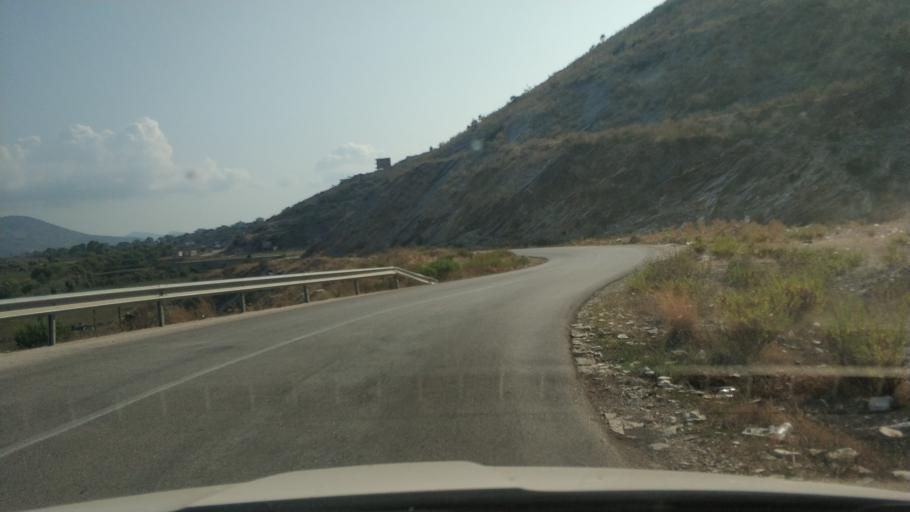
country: AL
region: Vlore
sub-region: Rrethi i Sarandes
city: Sarande
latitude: 39.8583
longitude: 20.0356
